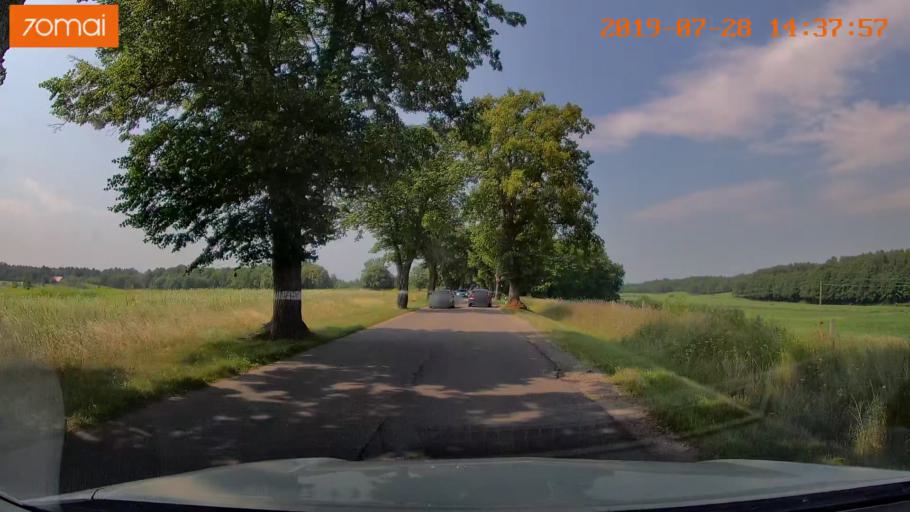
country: RU
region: Kaliningrad
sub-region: Gorod Kaliningrad
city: Yantarnyy
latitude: 54.8425
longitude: 19.9905
